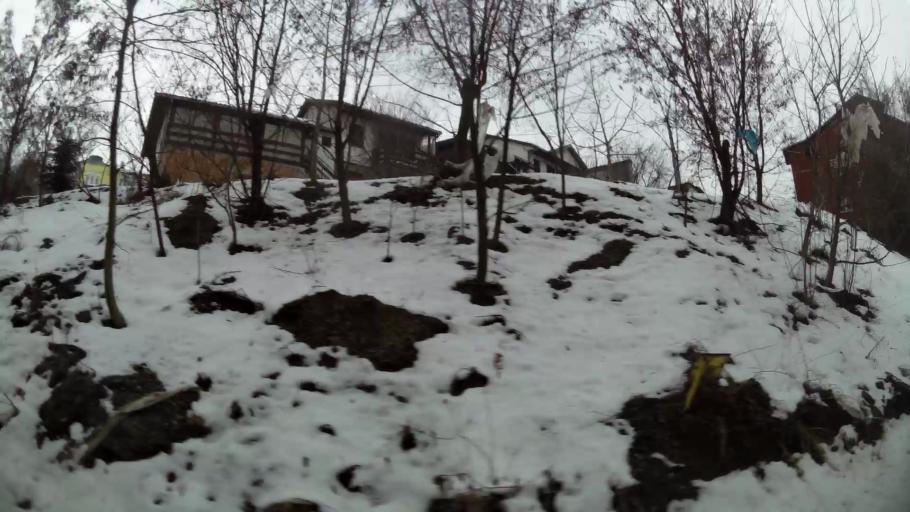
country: RS
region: Central Serbia
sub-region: Belgrade
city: Zvezdara
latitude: 44.7692
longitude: 20.5113
